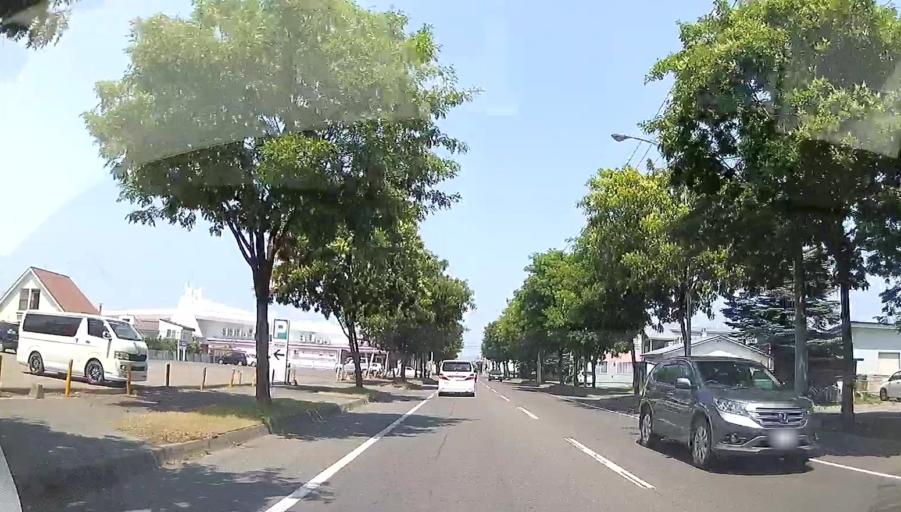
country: JP
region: Hokkaido
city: Obihiro
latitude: 42.8897
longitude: 143.2016
